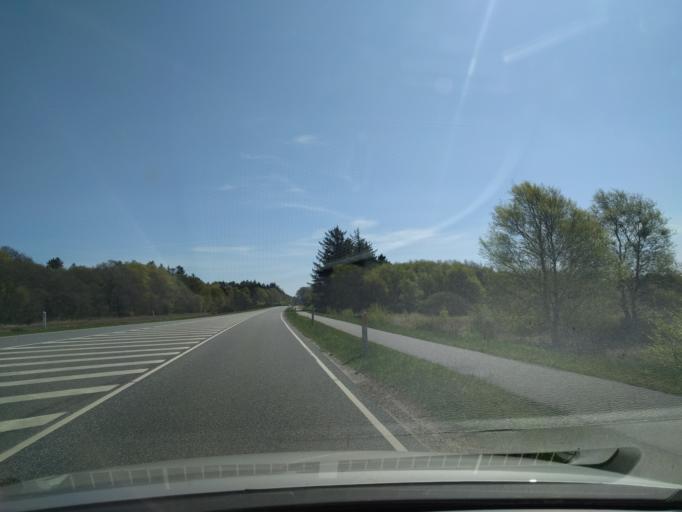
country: DK
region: Central Jutland
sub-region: Ringkobing-Skjern Kommune
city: Ringkobing
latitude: 56.0864
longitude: 8.3001
